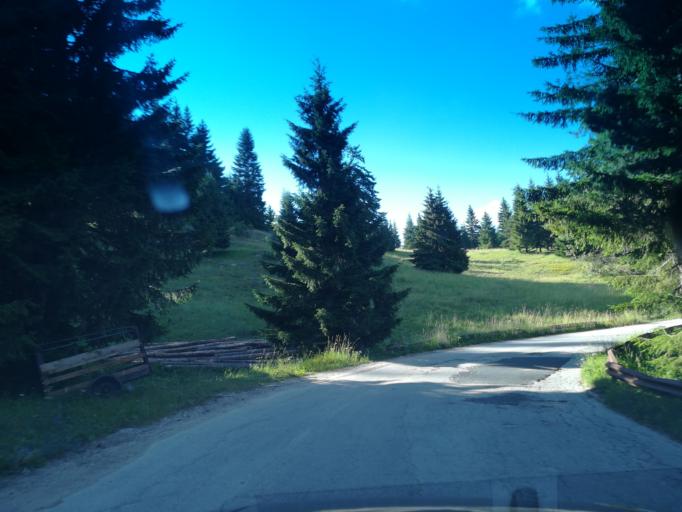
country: BG
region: Smolyan
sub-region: Obshtina Chepelare
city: Chepelare
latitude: 41.6916
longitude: 24.7560
